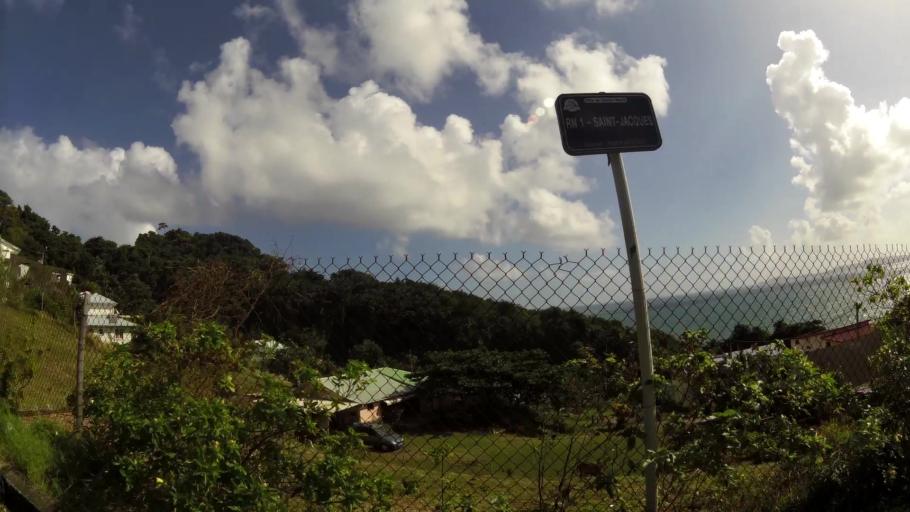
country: MQ
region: Martinique
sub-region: Martinique
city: Sainte-Marie
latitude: 14.8025
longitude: -61.0074
